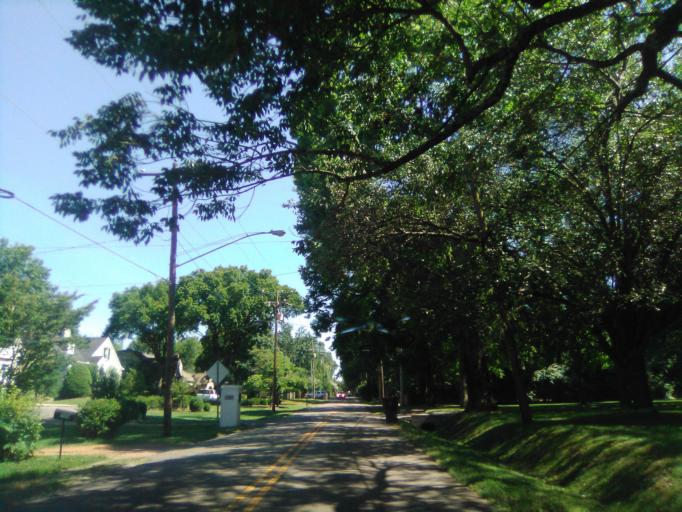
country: US
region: Tennessee
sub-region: Davidson County
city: Belle Meade
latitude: 36.1205
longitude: -86.8304
